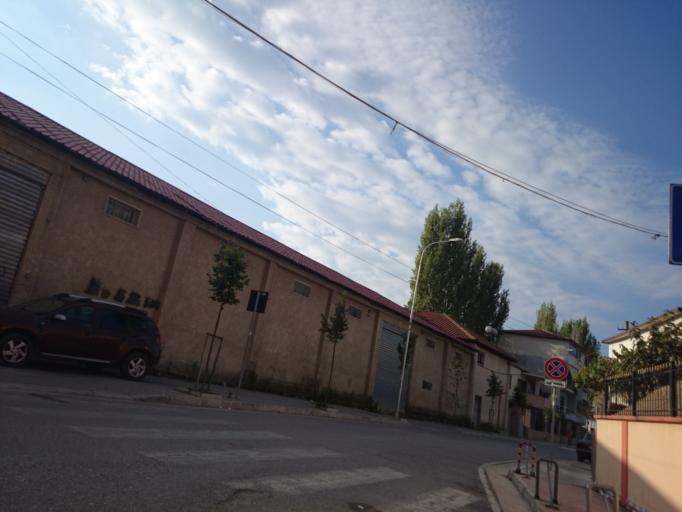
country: AL
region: Tirane
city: Tirana
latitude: 41.3181
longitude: 19.8023
